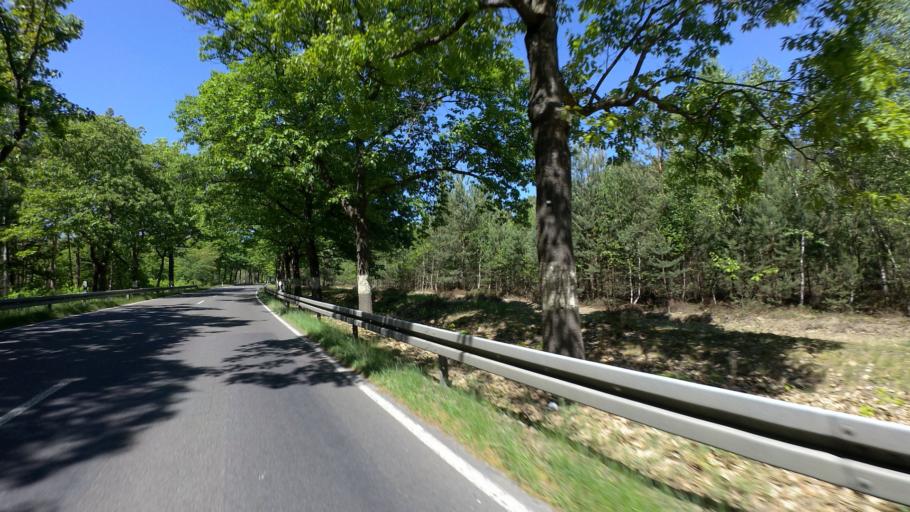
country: DE
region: Brandenburg
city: Drehnow
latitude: 51.9011
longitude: 14.3566
